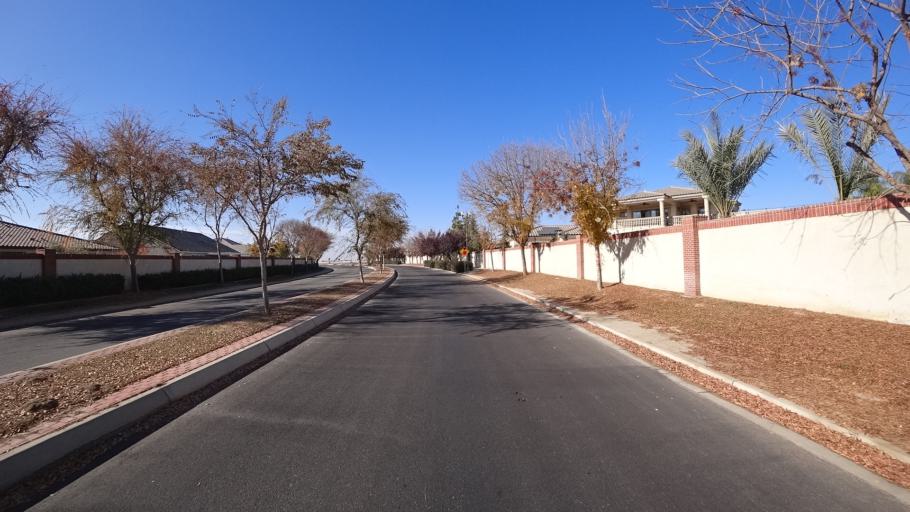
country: US
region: California
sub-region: Kern County
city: Rosedale
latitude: 35.3321
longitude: -119.1434
